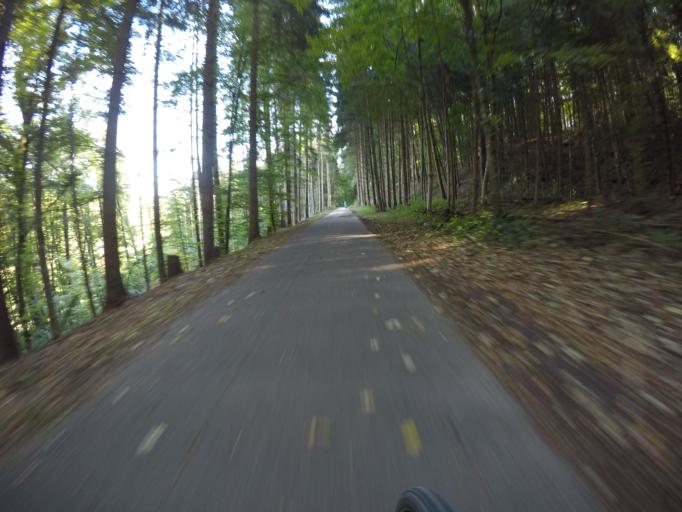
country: DE
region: Baden-Wuerttemberg
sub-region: Regierungsbezirk Stuttgart
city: Steinenbronn
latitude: 48.6736
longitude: 9.1279
